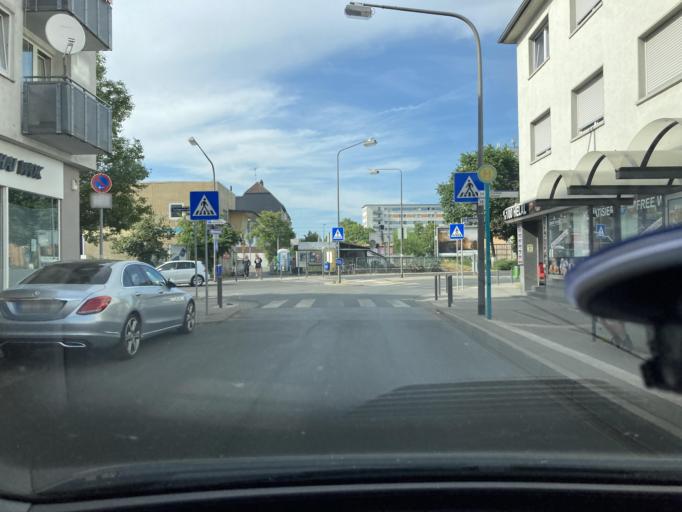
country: DE
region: Hesse
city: Niederrad
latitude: 50.0936
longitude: 8.6071
